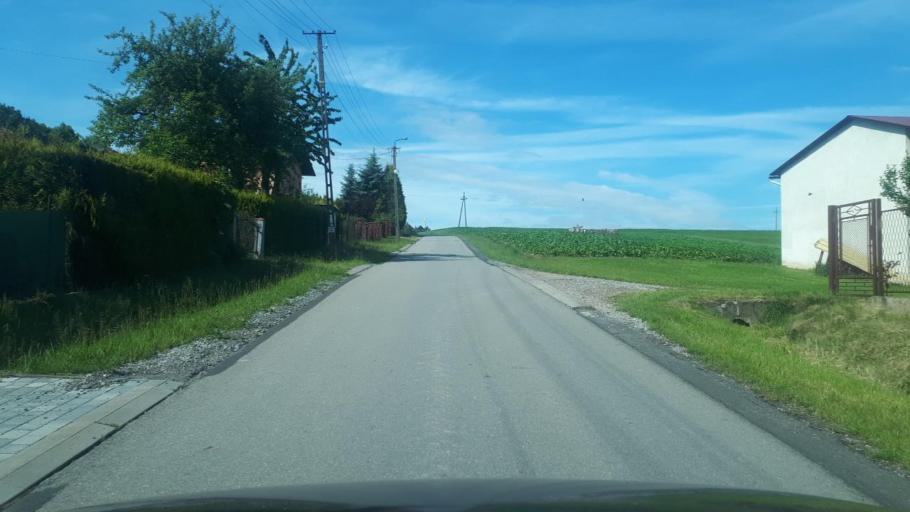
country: PL
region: Silesian Voivodeship
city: Janowice
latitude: 49.9046
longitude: 19.1143
